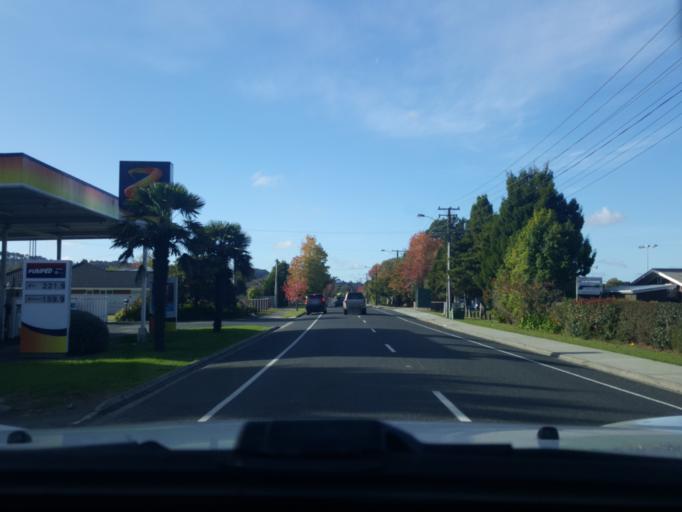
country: NZ
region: Auckland
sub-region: Auckland
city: Rosebank
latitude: -36.7616
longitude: 174.5882
